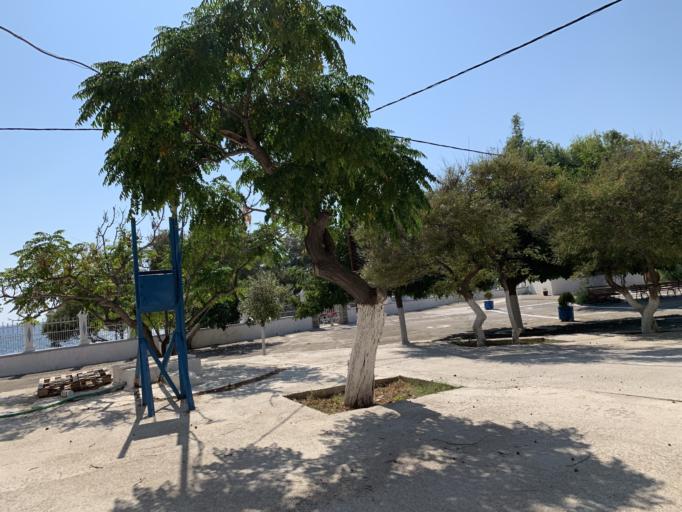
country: GR
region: North Aegean
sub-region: Chios
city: Vrontados
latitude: 38.4796
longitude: 25.8874
